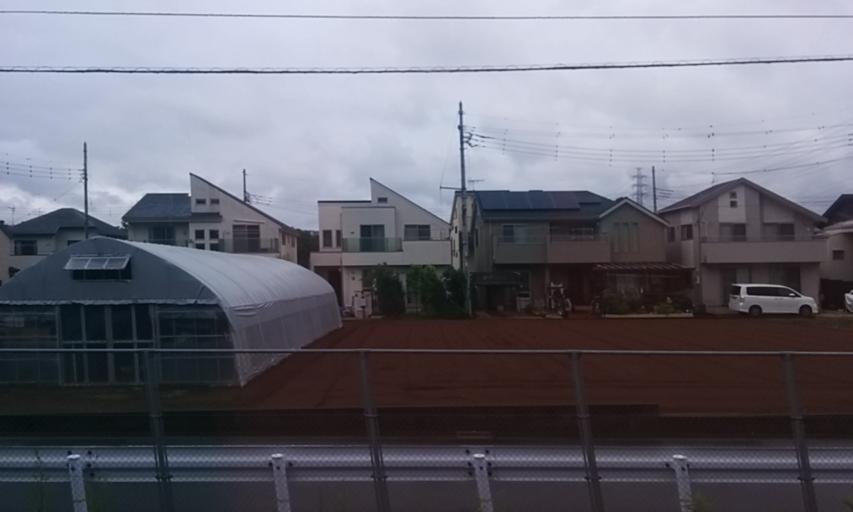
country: JP
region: Tokyo
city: Hino
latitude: 35.6486
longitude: 139.3812
